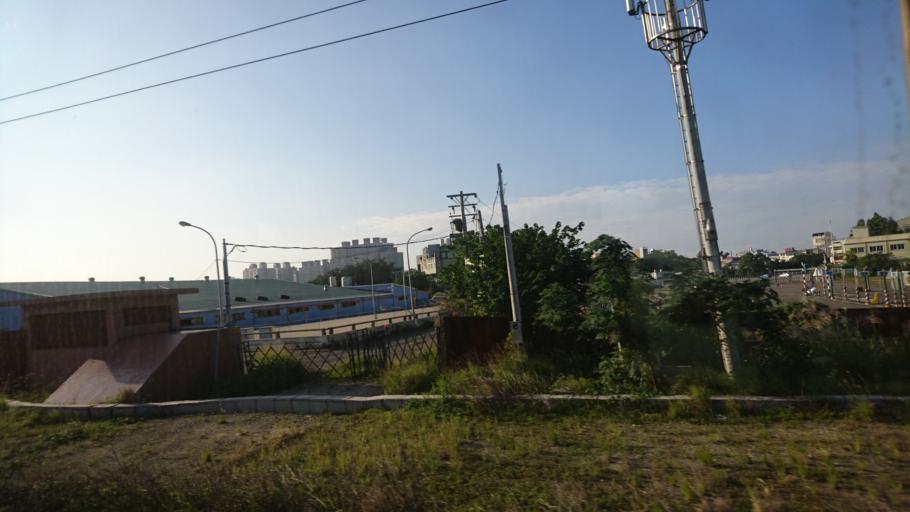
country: TW
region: Taiwan
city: Taoyuan City
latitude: 24.9632
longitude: 121.2445
